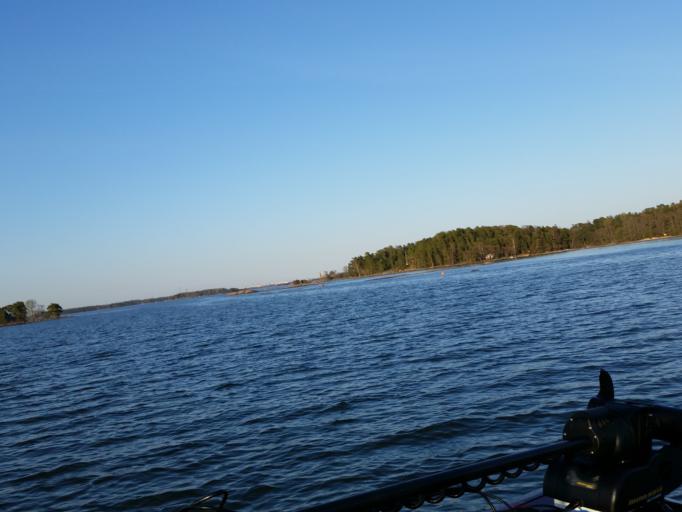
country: FI
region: Uusimaa
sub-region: Helsinki
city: Koukkuniemi
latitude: 60.1364
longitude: 24.7658
